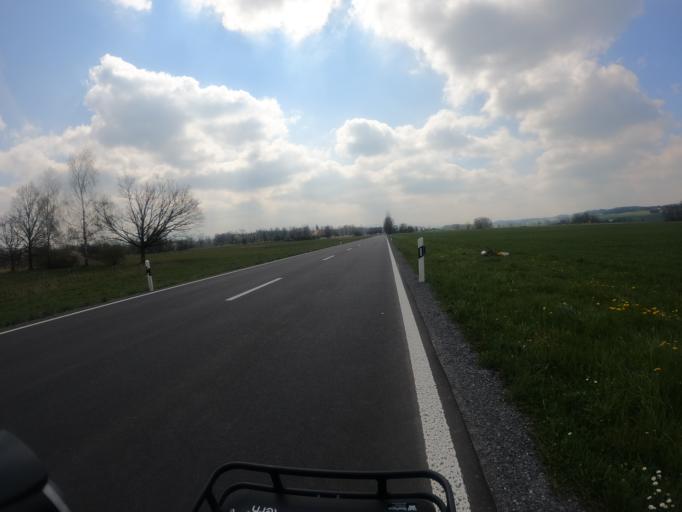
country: CH
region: Zurich
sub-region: Bezirk Affoltern
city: Obfelden / Oberlunnern
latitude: 47.2289
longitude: 8.4151
